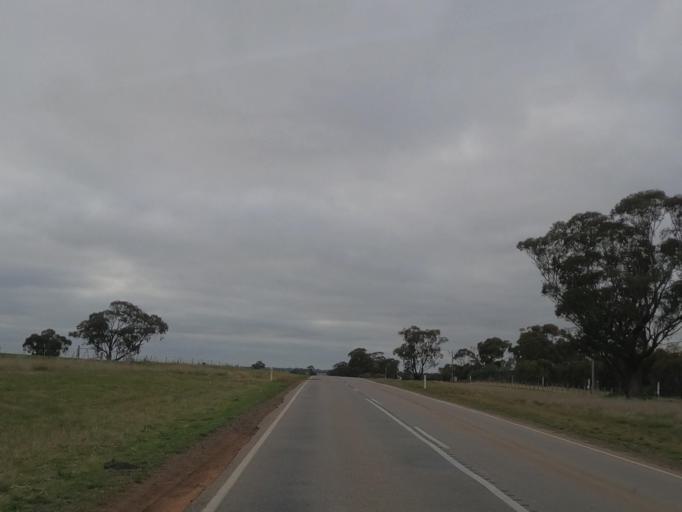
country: AU
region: Victoria
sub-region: Greater Bendigo
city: Long Gully
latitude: -36.4921
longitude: 143.9575
